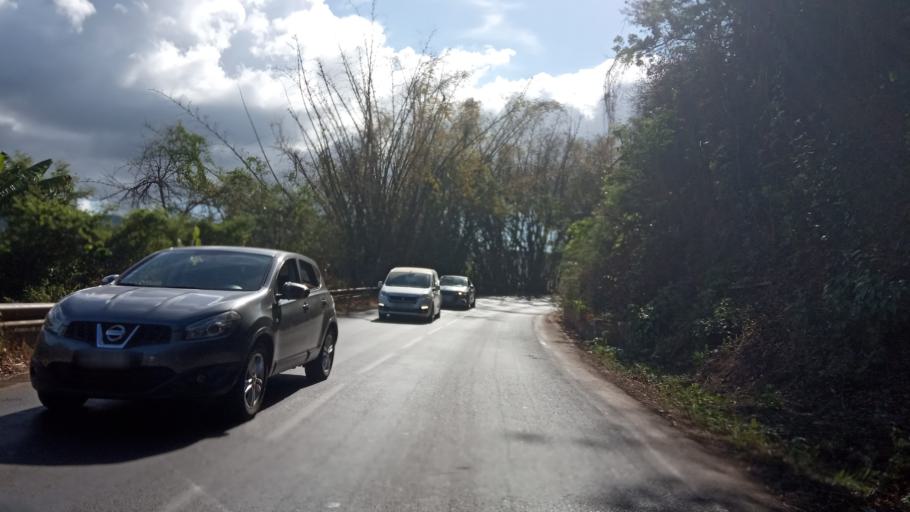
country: YT
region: Dembeni
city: Dembeni
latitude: -12.8379
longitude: 45.1833
